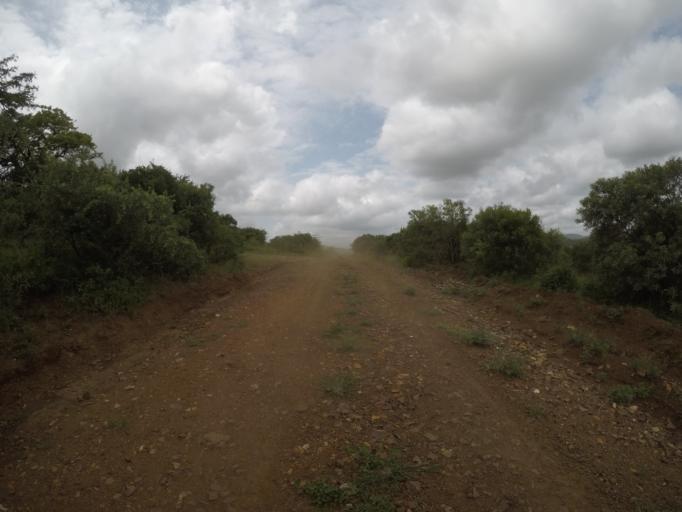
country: ZA
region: KwaZulu-Natal
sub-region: uThungulu District Municipality
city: Empangeni
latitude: -28.5849
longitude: 31.8685
